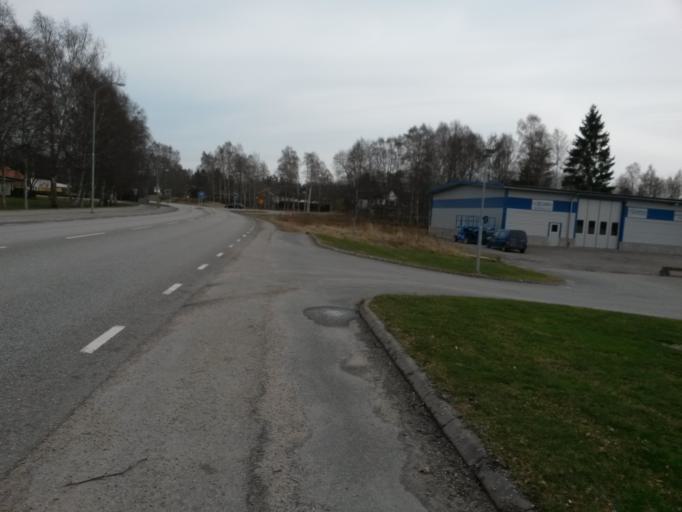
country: SE
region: Vaestra Goetaland
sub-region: Herrljunga Kommun
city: Herrljunga
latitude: 58.0730
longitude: 13.0228
